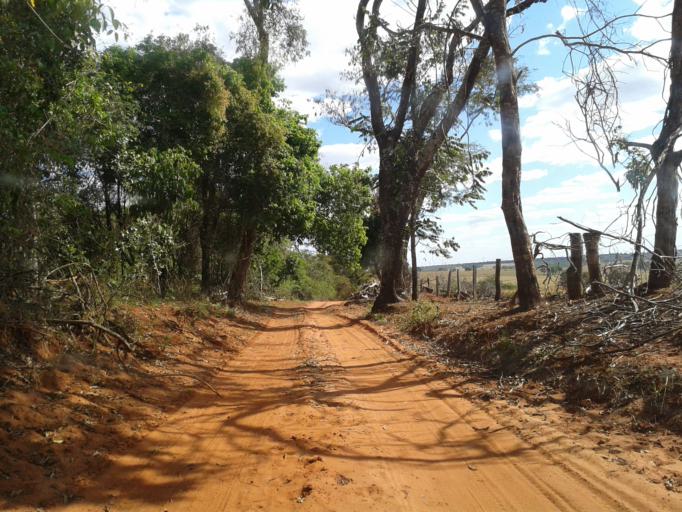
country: BR
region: Minas Gerais
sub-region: Centralina
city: Centralina
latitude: -18.7577
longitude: -49.0810
